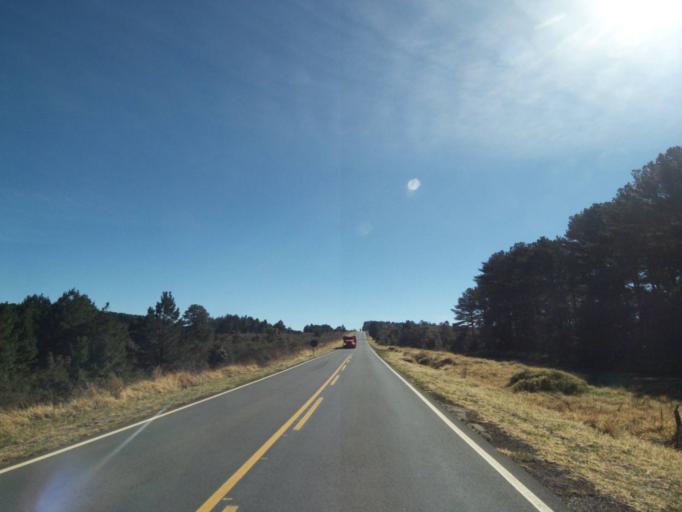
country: BR
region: Parana
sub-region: Castro
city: Castro
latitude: -24.7225
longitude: -50.1859
